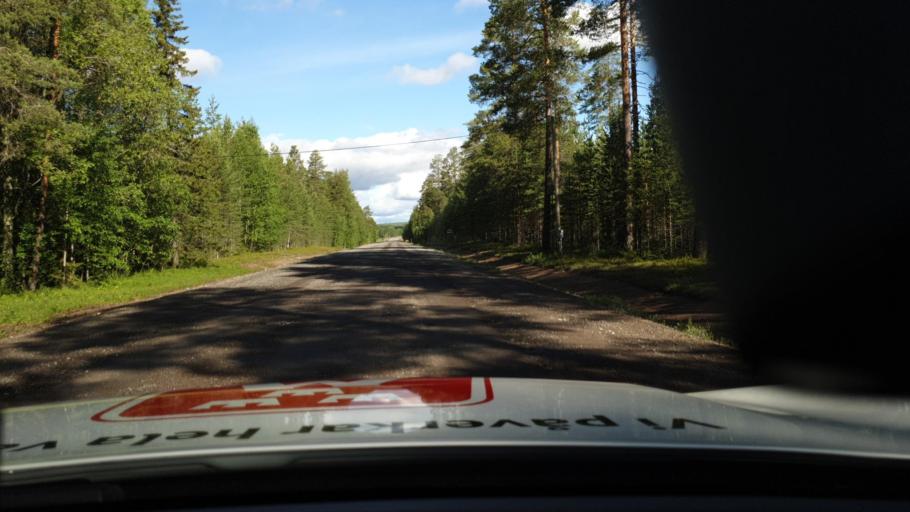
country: SE
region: Norrbotten
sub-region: Bodens Kommun
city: Boden
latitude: 65.8791
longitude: 21.4047
